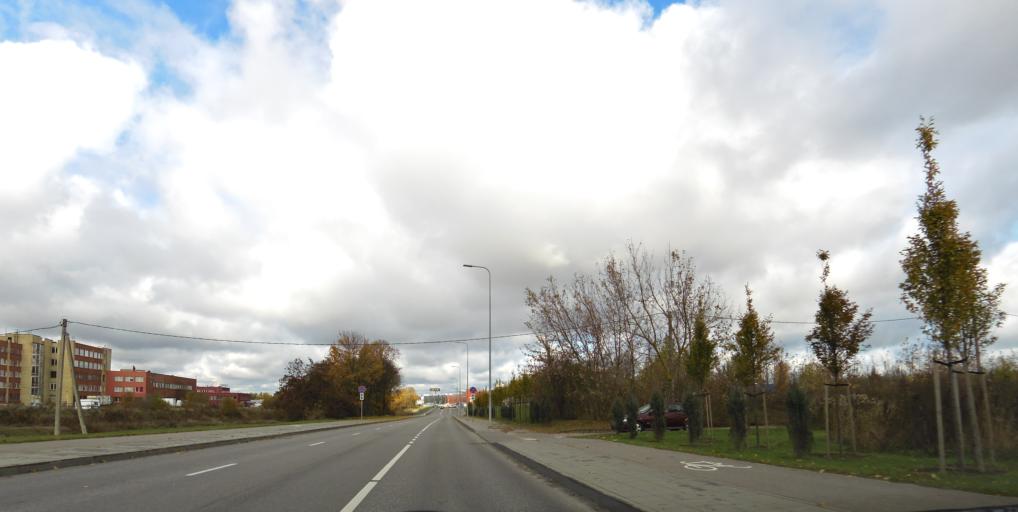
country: LT
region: Vilnius County
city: Naujamiestis
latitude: 54.6471
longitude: 25.2764
